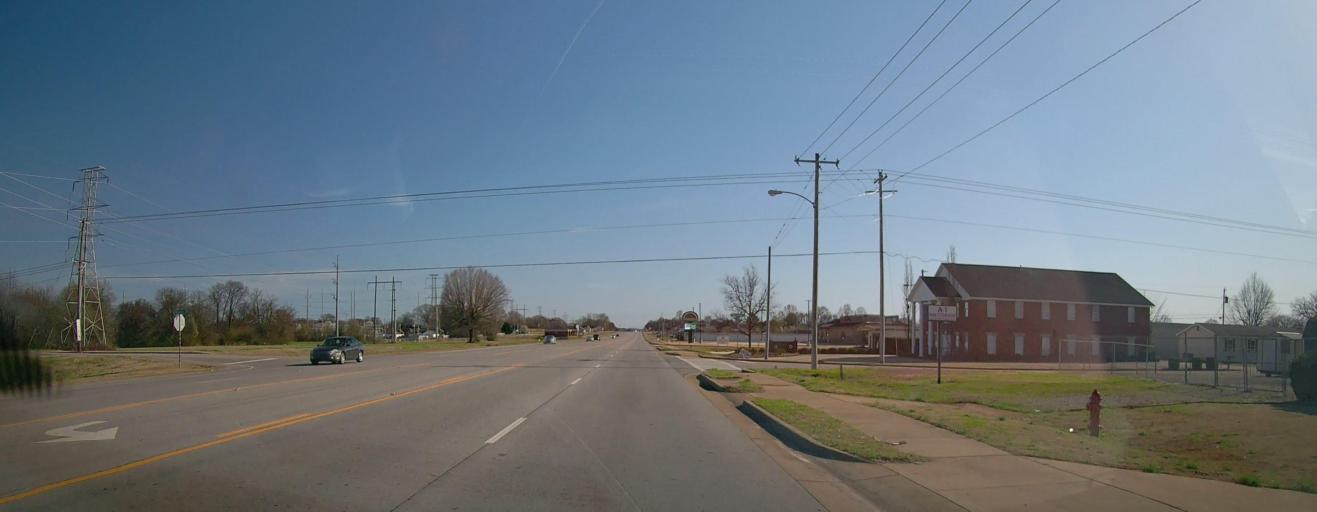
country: US
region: Alabama
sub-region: Colbert County
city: Muscle Shoals
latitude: 34.7409
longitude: -87.6354
